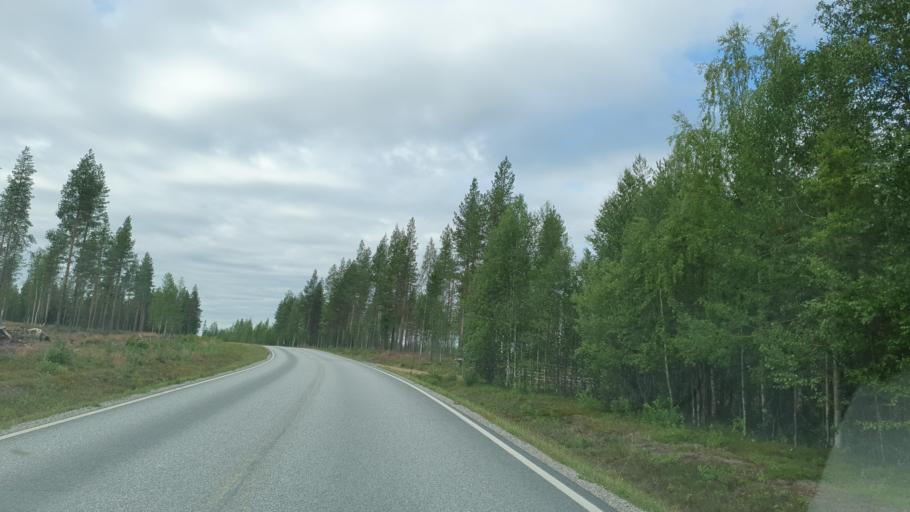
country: FI
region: Lapland
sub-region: Tunturi-Lappi
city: Kittilae
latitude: 67.6117
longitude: 25.2476
